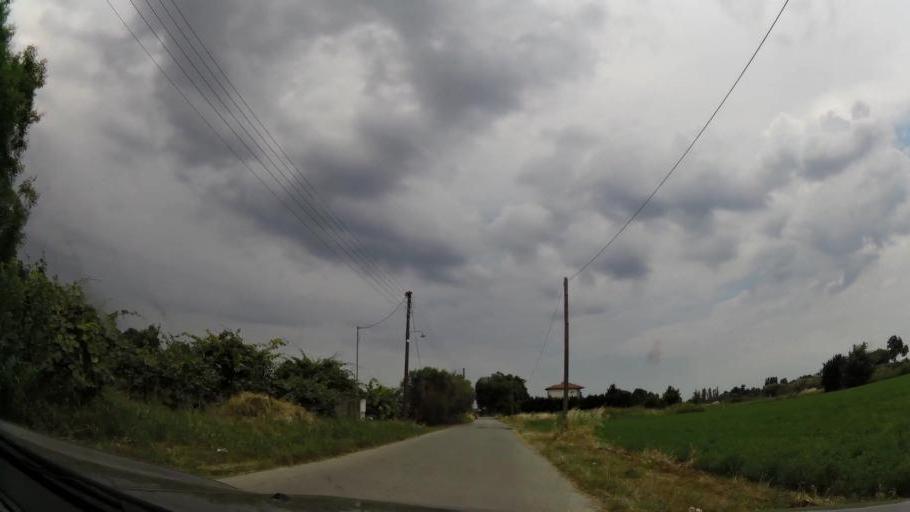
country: GR
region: Central Macedonia
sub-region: Nomos Pierias
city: Kallithea
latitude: 40.2740
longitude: 22.5839
